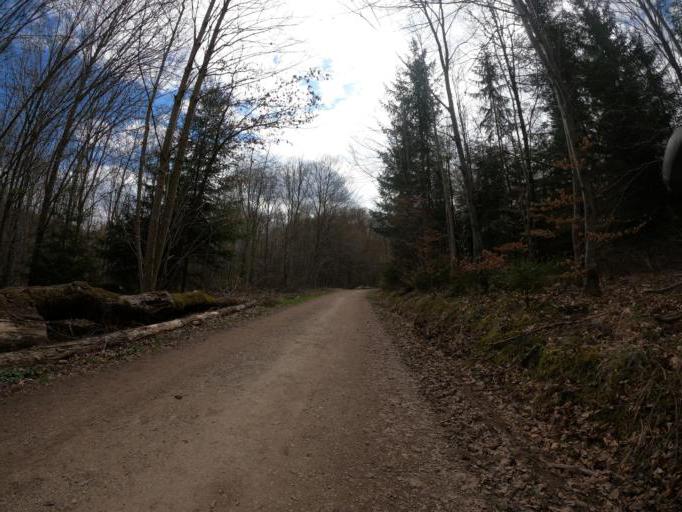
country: DE
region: Baden-Wuerttemberg
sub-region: Tuebingen Region
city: Gomaringen
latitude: 48.4793
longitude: 9.0791
